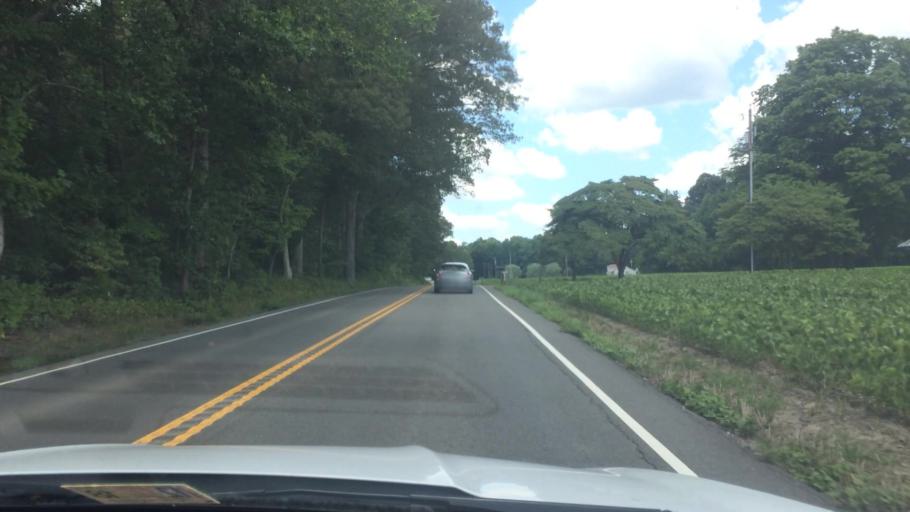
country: US
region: Virginia
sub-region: King William County
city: West Point
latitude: 37.6011
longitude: -76.7681
